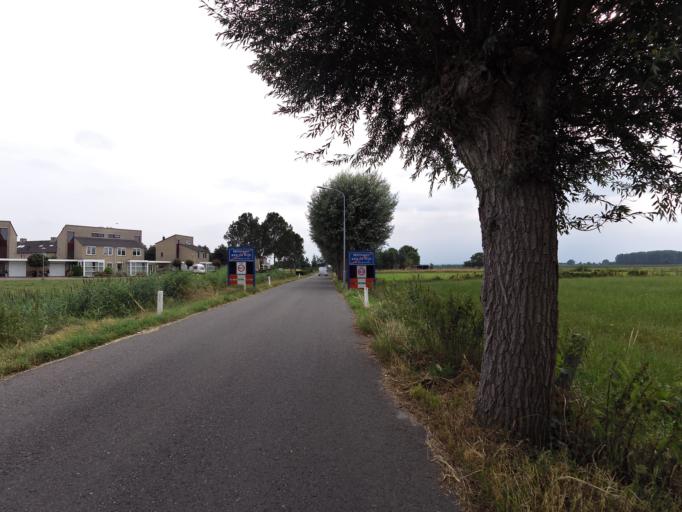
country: NL
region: Gelderland
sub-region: Gemeente Zevenaar
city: Zevenaar
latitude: 51.8627
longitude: 6.0378
